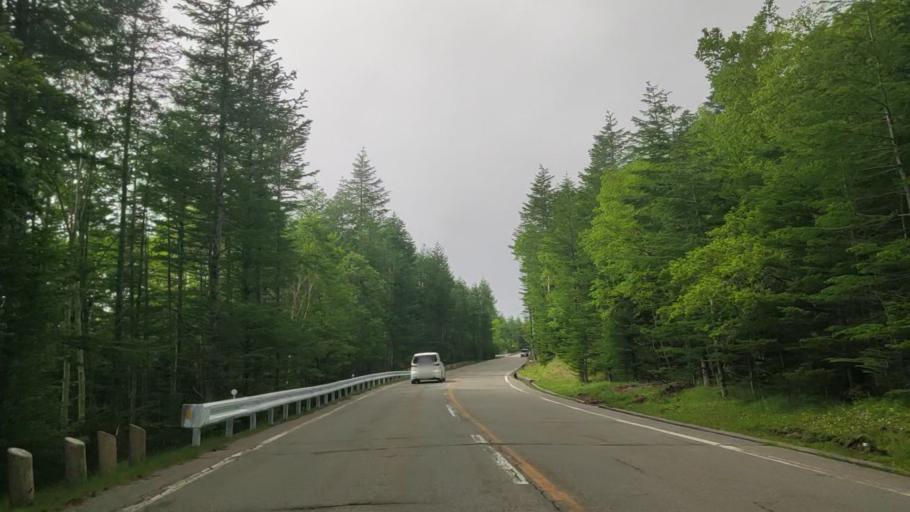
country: JP
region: Yamanashi
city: Fujikawaguchiko
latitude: 35.3767
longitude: 138.6929
